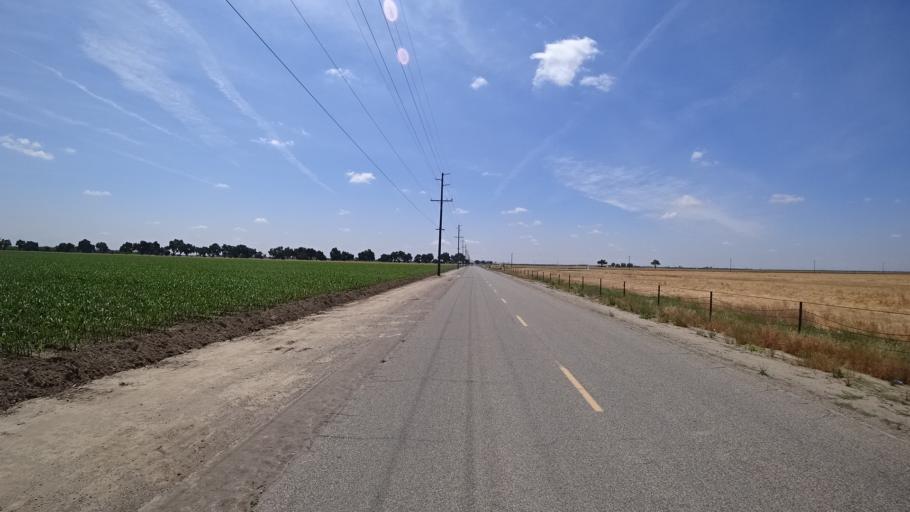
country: US
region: California
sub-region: Tulare County
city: Goshen
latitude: 36.2933
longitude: -119.4743
